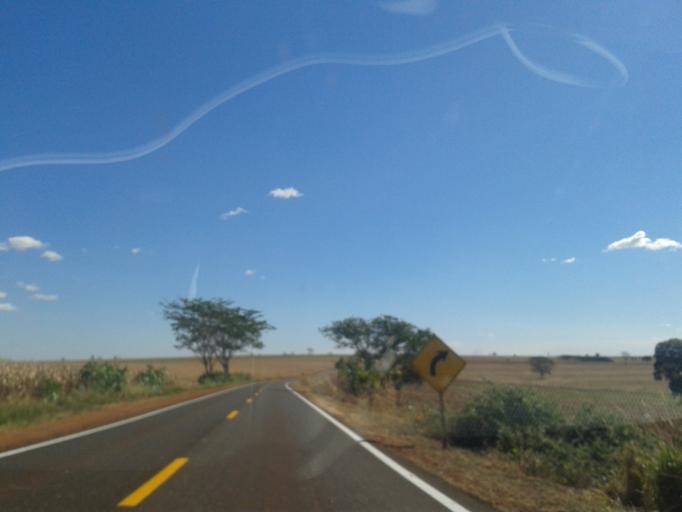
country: BR
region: Minas Gerais
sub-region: Capinopolis
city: Capinopolis
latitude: -18.6930
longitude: -49.4854
